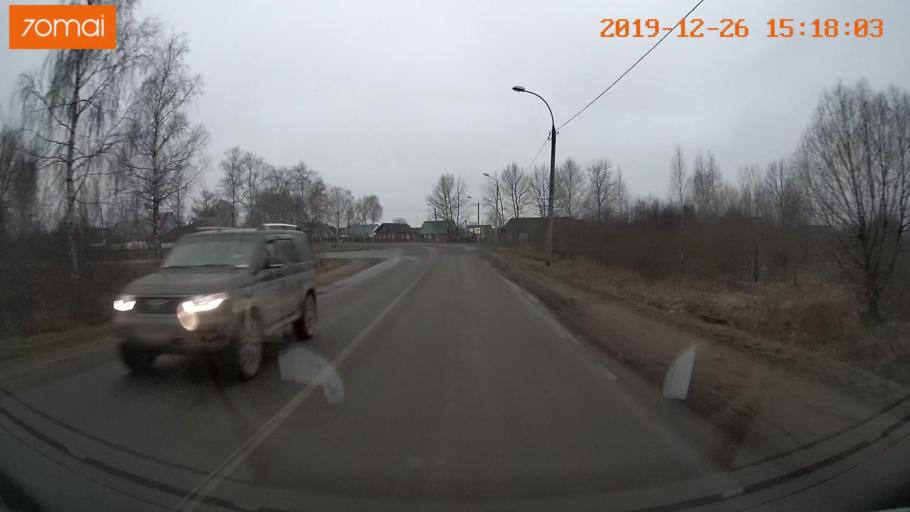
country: RU
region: Jaroslavl
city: Rybinsk
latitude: 58.0723
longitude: 38.8447
